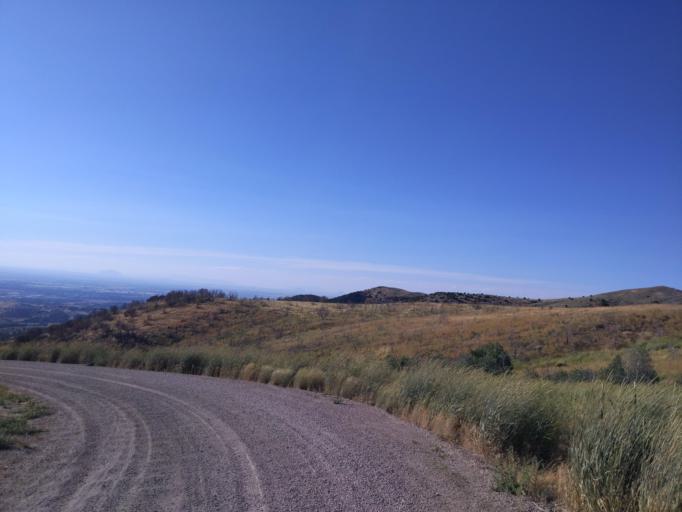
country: US
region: Idaho
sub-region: Bannock County
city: Pocatello
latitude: 42.8504
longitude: -112.3713
